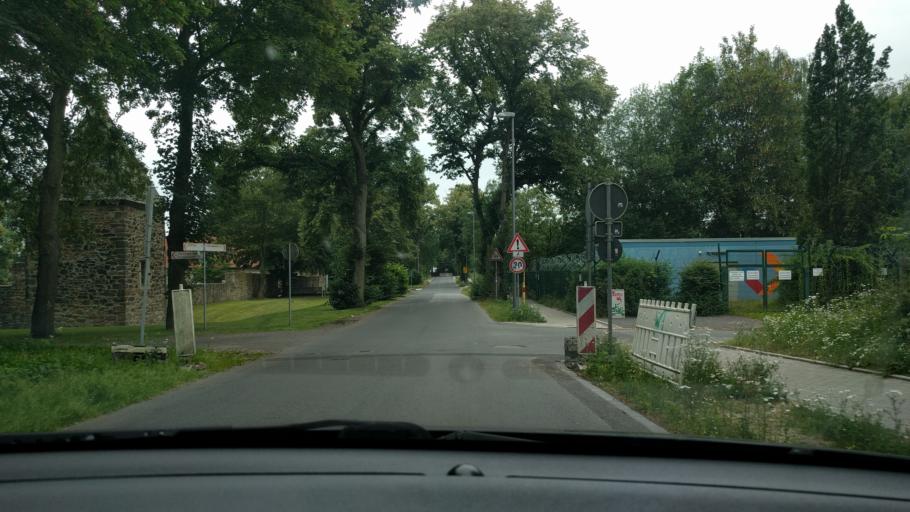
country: DE
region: North Rhine-Westphalia
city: Witten
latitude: 51.4773
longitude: 7.3280
